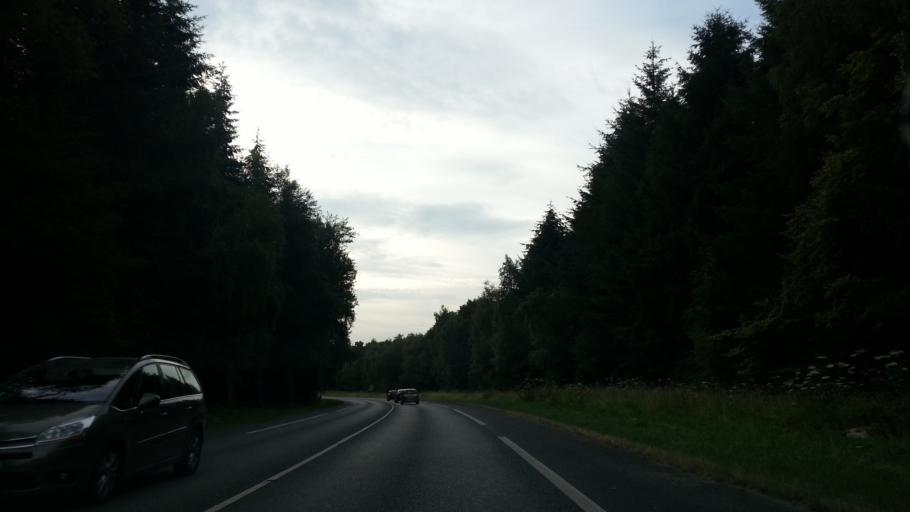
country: FR
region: Picardie
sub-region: Departement de l'Oise
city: Creil
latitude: 49.2424
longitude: 2.4985
